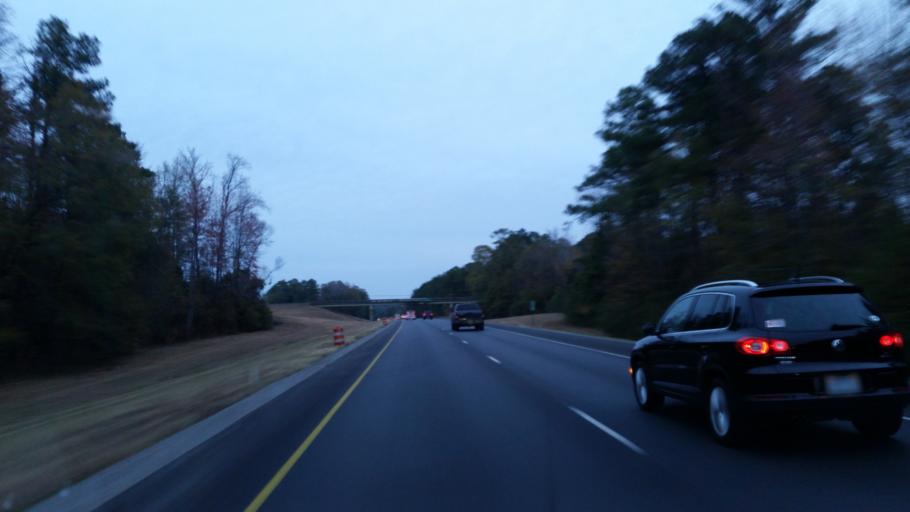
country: US
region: Alabama
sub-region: Hale County
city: Moundville
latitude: 33.0022
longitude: -87.7668
